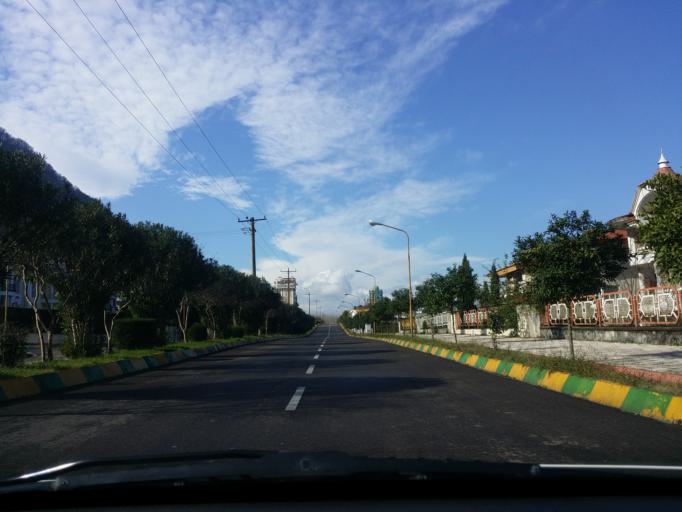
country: IR
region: Mazandaran
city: Chalus
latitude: 36.6666
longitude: 51.3165
